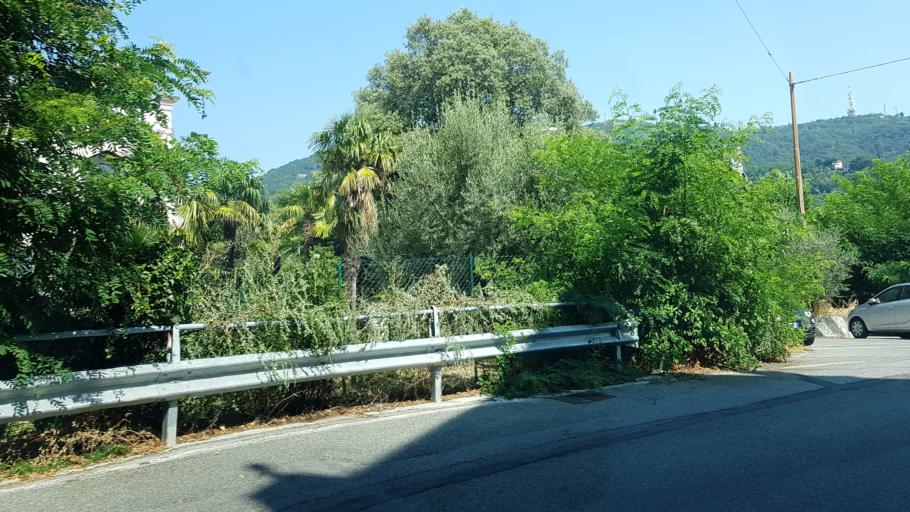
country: IT
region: Liguria
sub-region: Provincia di Genova
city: Genoa
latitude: 44.4409
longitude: 8.8972
